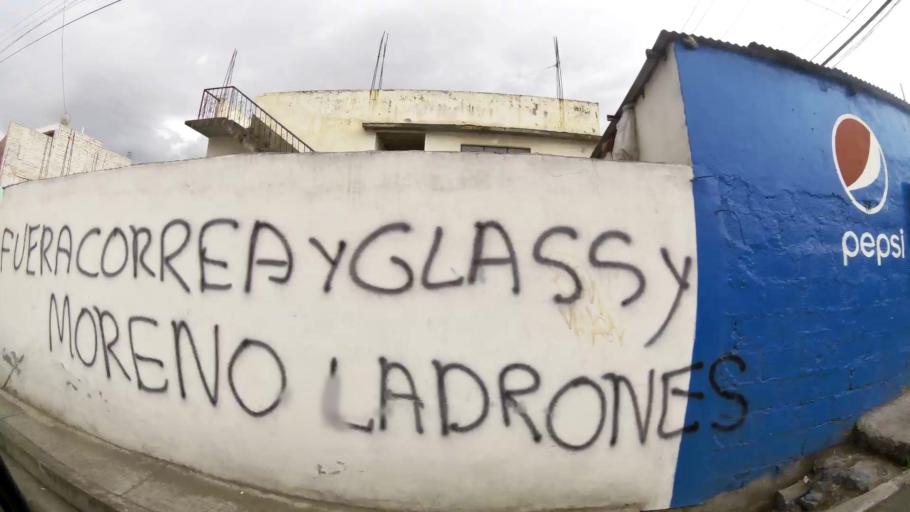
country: EC
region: Tungurahua
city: Ambato
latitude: -1.2782
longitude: -78.6246
